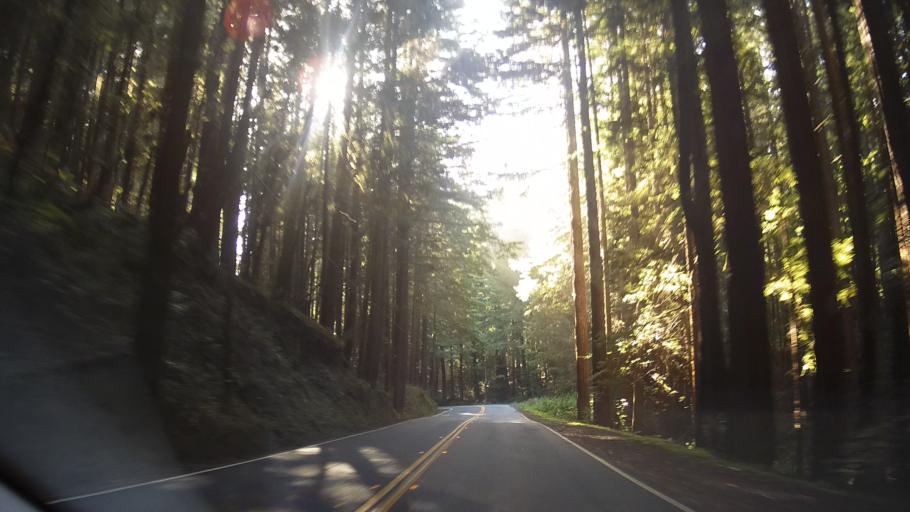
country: US
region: California
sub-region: Mendocino County
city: Brooktrails
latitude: 39.3482
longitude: -123.5706
